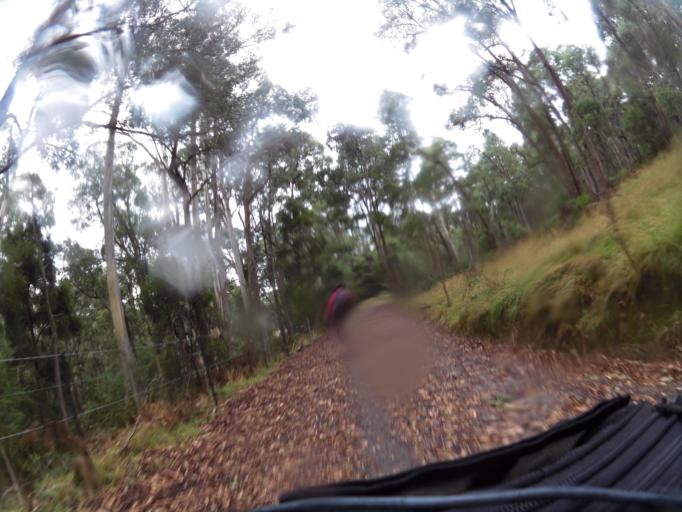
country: AU
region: New South Wales
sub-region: Greater Hume Shire
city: Holbrook
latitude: -36.1638
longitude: 147.4852
